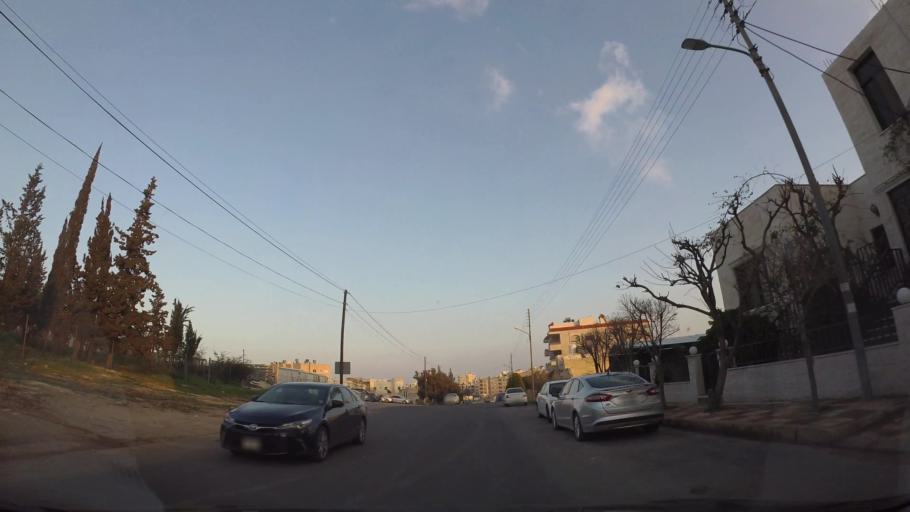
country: JO
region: Amman
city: Amman
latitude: 31.9933
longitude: 35.9542
